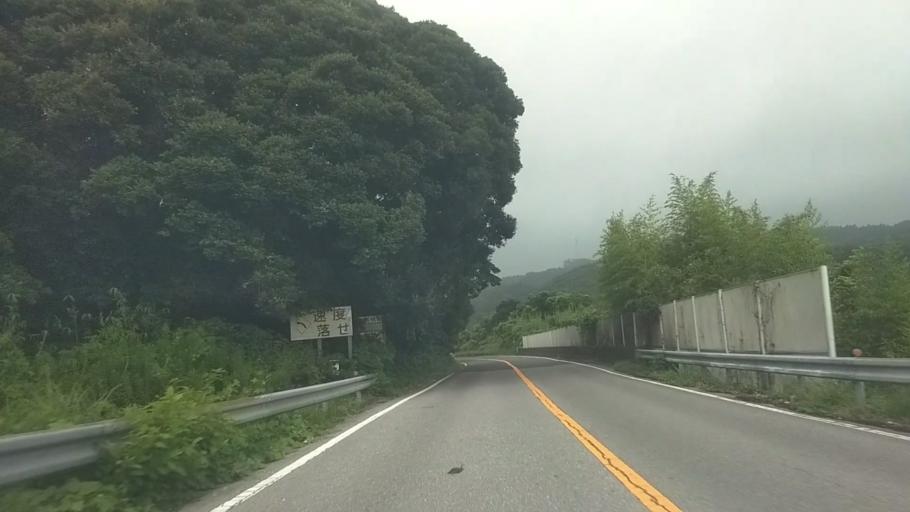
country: JP
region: Chiba
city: Katsuura
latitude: 35.1660
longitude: 140.3262
